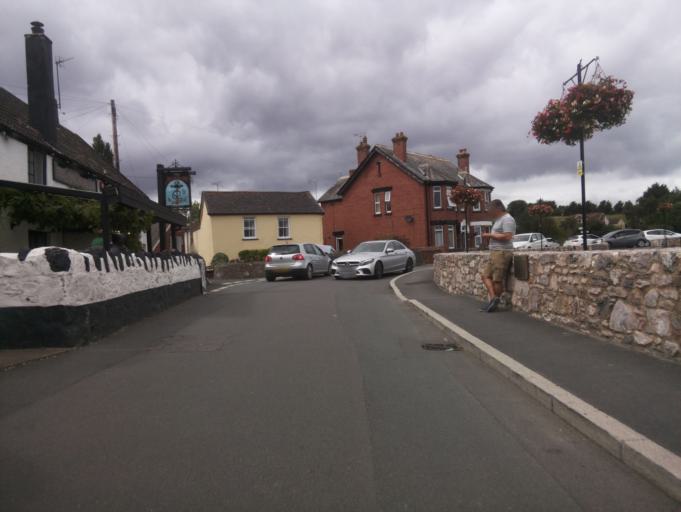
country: GB
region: England
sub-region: Devon
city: Starcross
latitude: 50.6169
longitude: -3.4488
